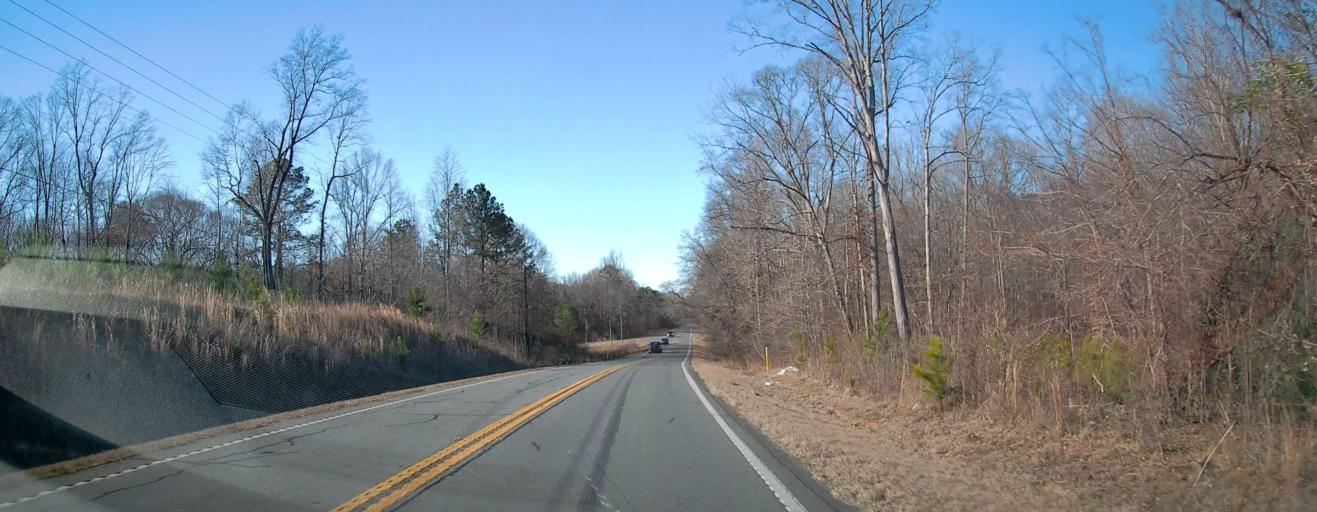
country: US
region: Georgia
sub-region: Talbot County
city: Talbotton
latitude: 32.6959
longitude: -84.5483
